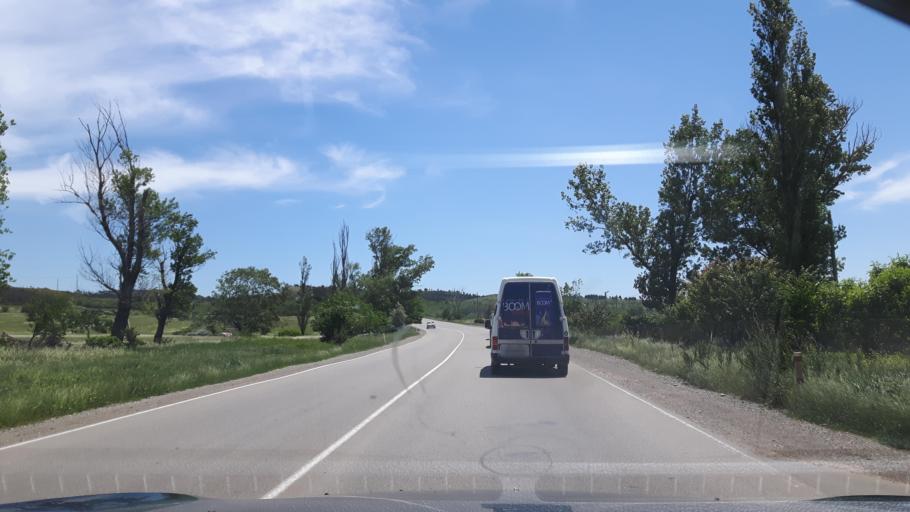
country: GE
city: Didi Lilo
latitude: 41.6930
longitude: 45.0645
